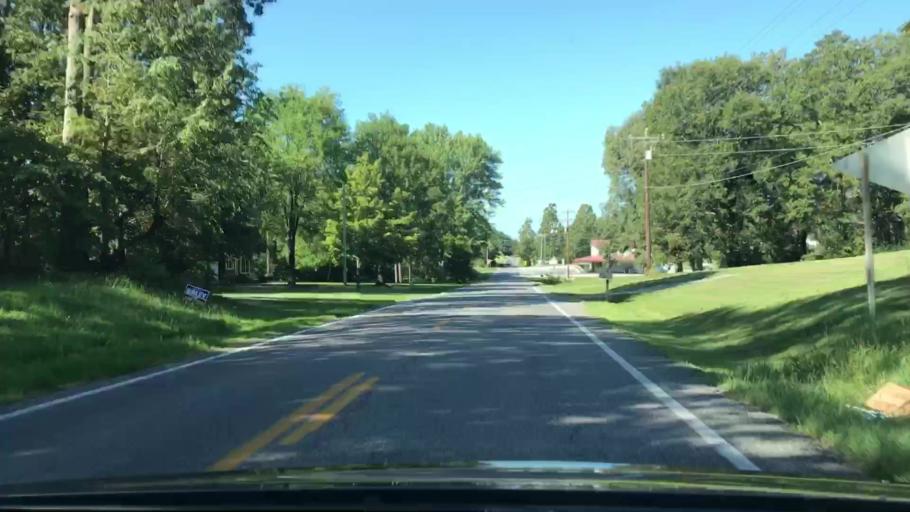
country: US
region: Kentucky
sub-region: Graves County
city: Mayfield
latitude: 36.7641
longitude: -88.5776
